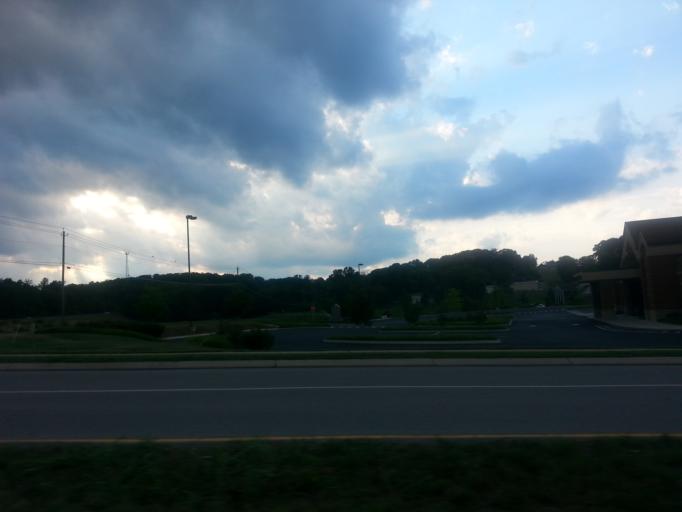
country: US
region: Tennessee
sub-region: Knox County
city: Knoxville
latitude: 36.0554
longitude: -84.0015
